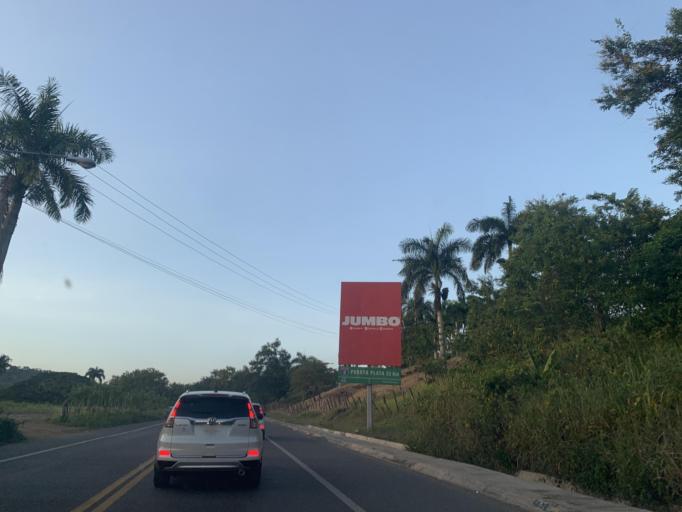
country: DO
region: Puerto Plata
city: Imbert
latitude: 19.7611
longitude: -70.8333
